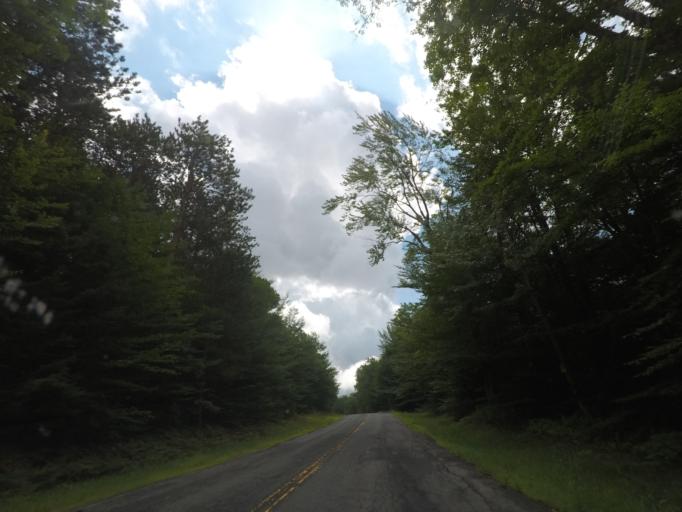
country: US
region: New York
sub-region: Rensselaer County
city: Averill Park
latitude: 42.6753
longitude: -73.4233
